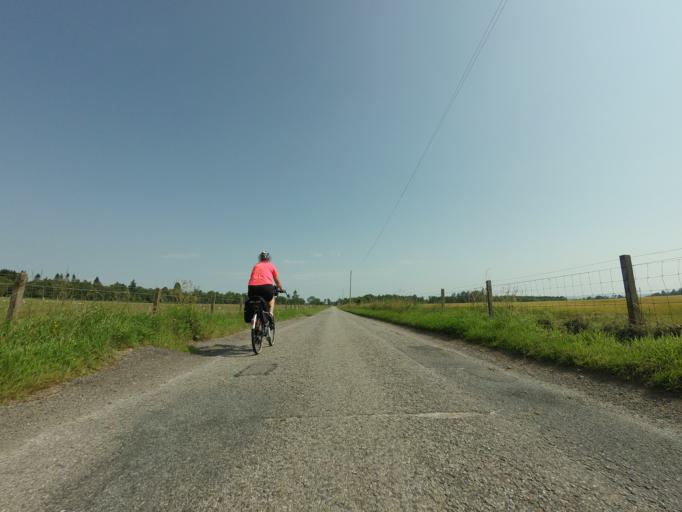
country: GB
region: Scotland
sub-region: Highland
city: Tain
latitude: 57.7937
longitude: -4.0788
